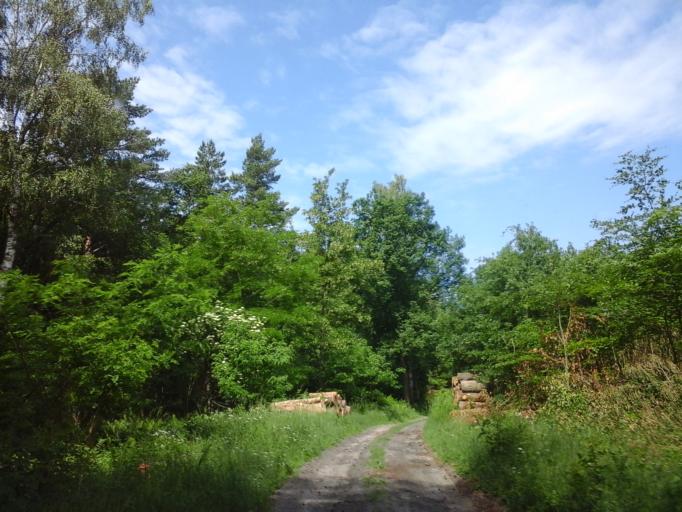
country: PL
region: West Pomeranian Voivodeship
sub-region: Powiat stargardzki
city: Dolice
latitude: 53.2186
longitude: 15.2537
